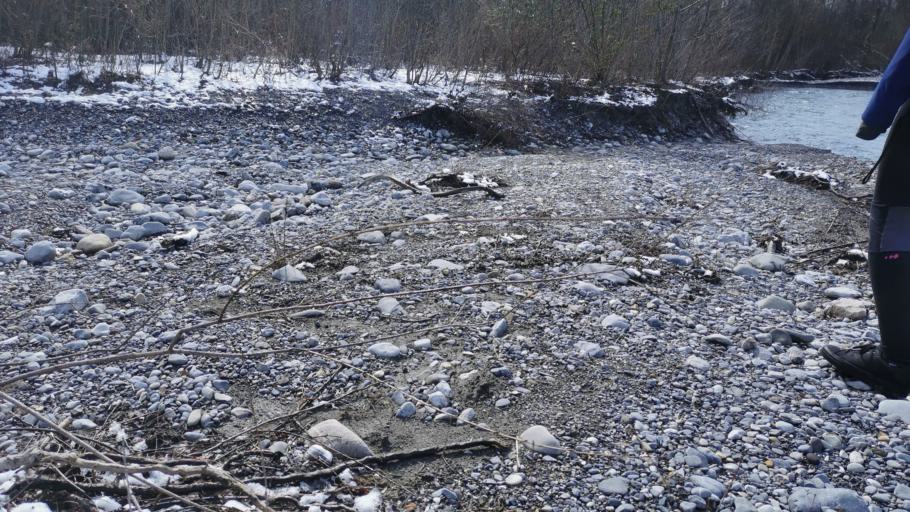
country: FR
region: Provence-Alpes-Cote d'Azur
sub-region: Departement des Alpes-de-Haute-Provence
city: Mallemoisson
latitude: 44.0621
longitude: 6.1711
